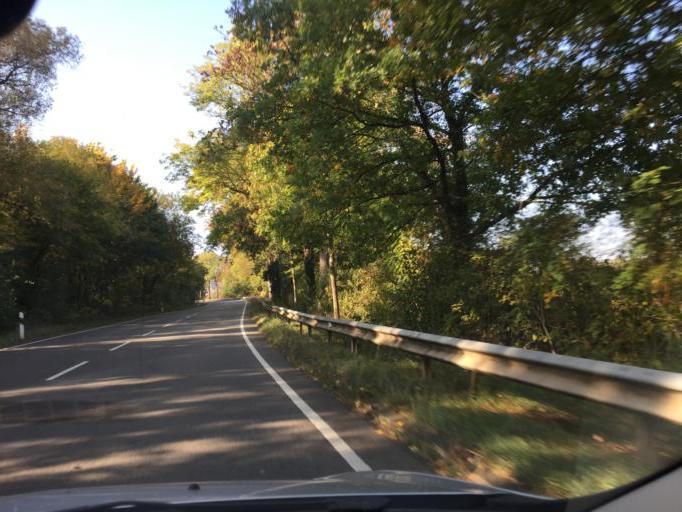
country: LU
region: Grevenmacher
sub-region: Canton de Remich
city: Bous
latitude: 49.5484
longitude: 6.3172
